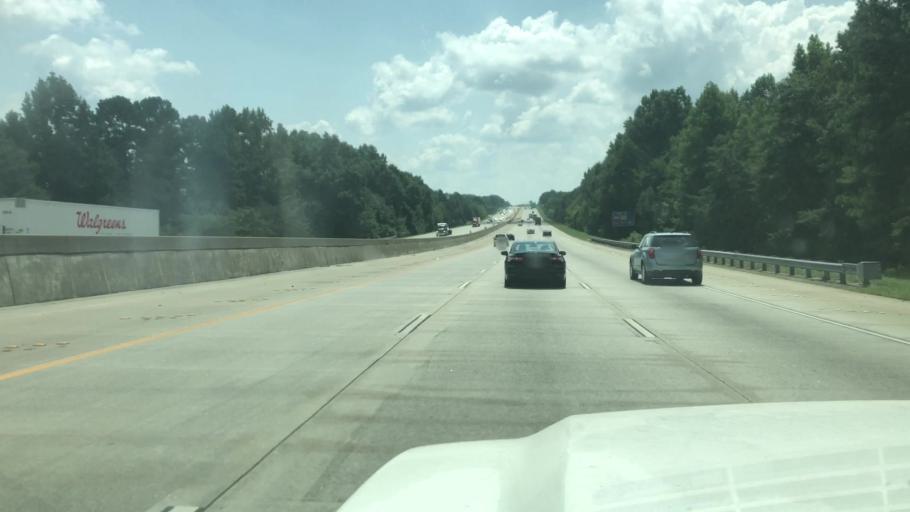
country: US
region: Georgia
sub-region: Coweta County
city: East Newnan
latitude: 33.3451
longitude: -84.7623
